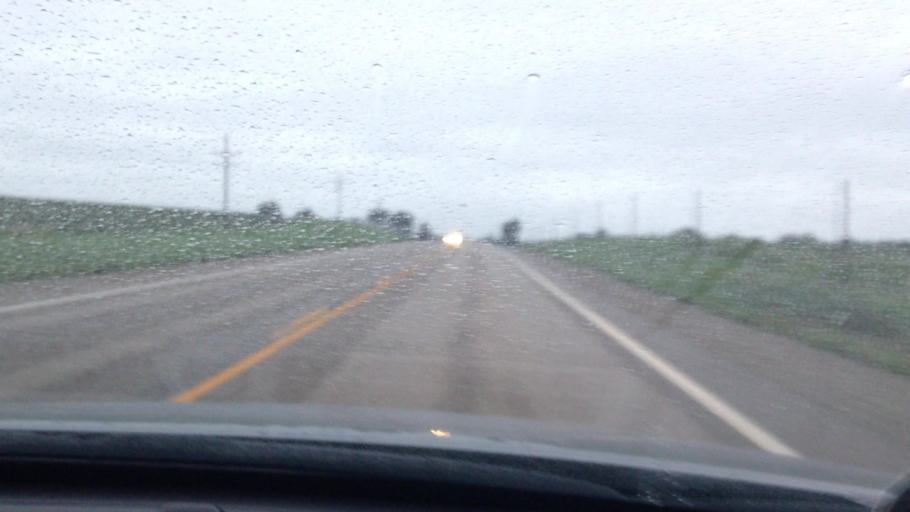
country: US
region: Kansas
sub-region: Brown County
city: Hiawatha
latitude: 39.8092
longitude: -95.5273
